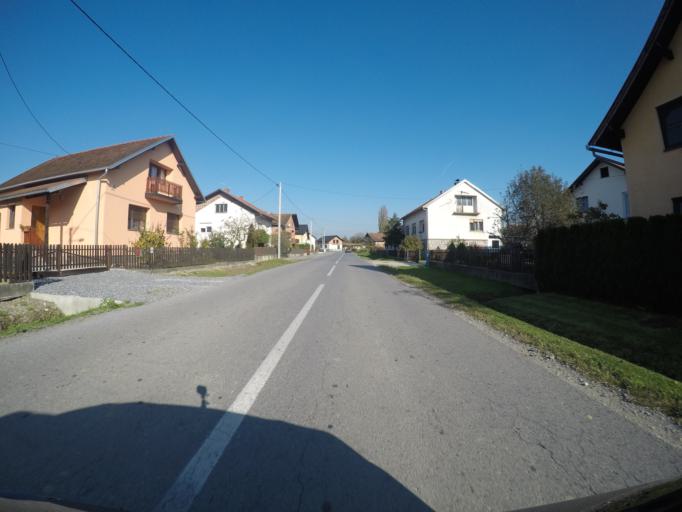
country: HR
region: Bjelovarsko-Bilogorska
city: Predavac
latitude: 45.9143
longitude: 16.7835
